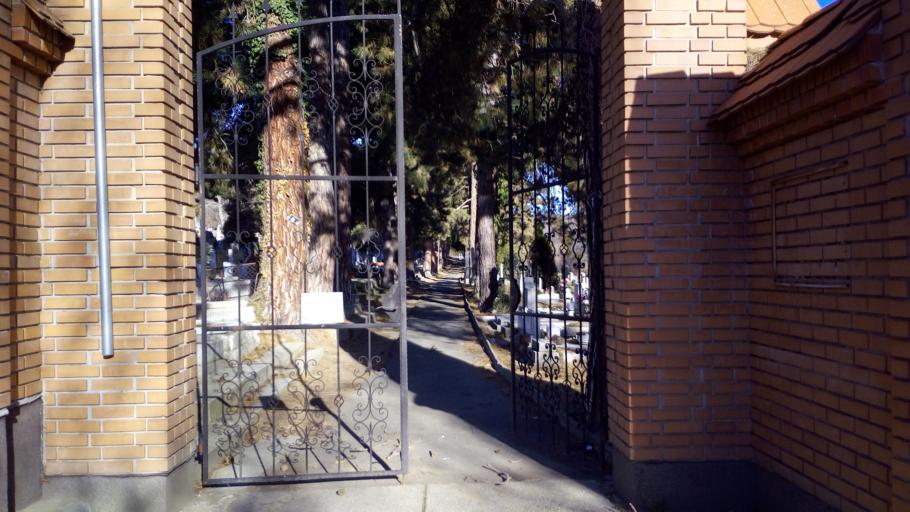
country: HU
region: Baranya
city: Pecs
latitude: 46.1142
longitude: 18.2465
